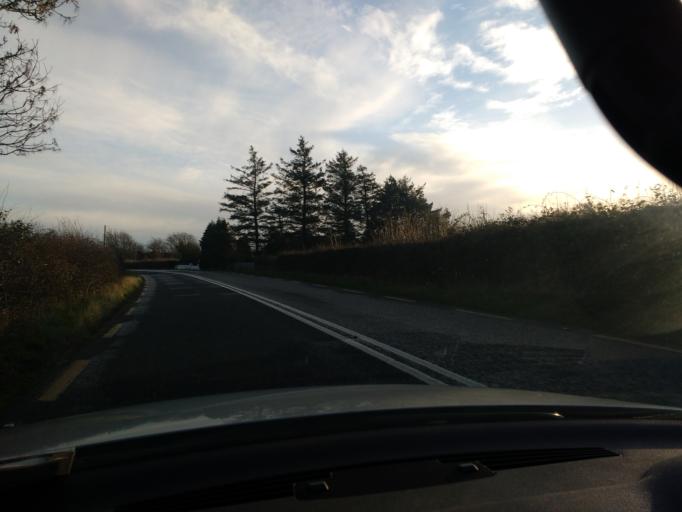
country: IE
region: Munster
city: Thurles
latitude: 52.6432
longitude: -7.7888
